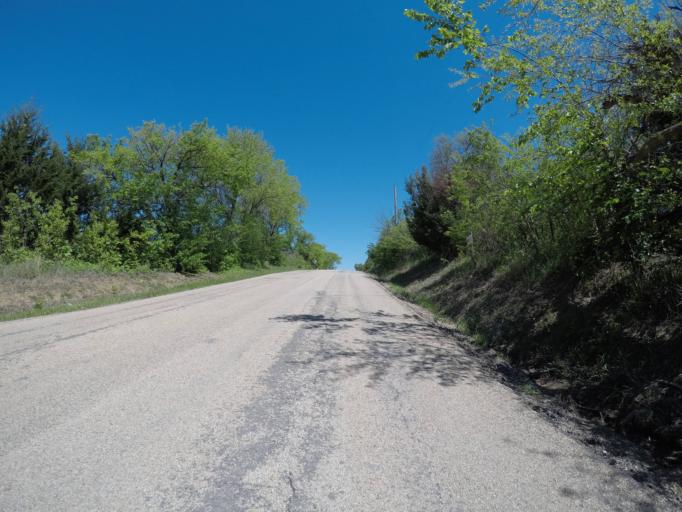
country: US
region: Kansas
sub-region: Shawnee County
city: Topeka
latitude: 38.9871
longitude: -95.5194
